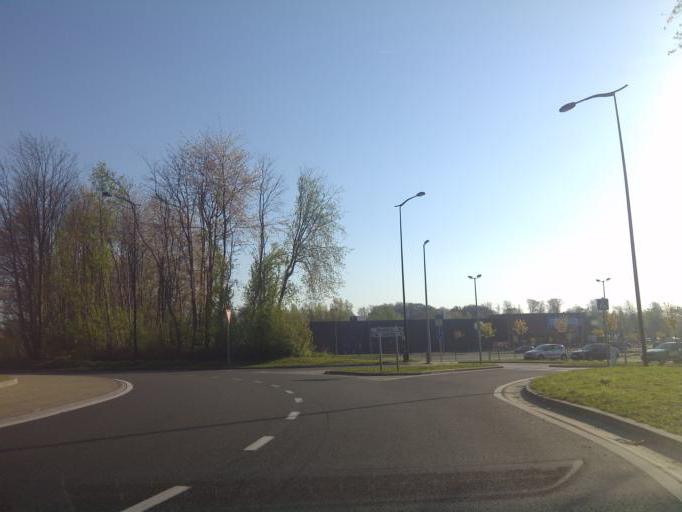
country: BE
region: Wallonia
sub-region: Province du Brabant Wallon
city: Louvain-la-Neuve
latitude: 50.6905
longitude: 4.6163
